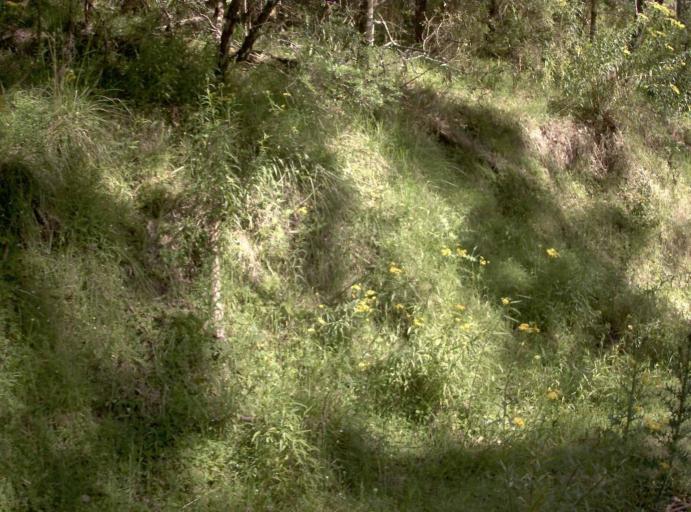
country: AU
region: New South Wales
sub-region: Bombala
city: Bombala
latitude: -37.3507
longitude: 148.6924
